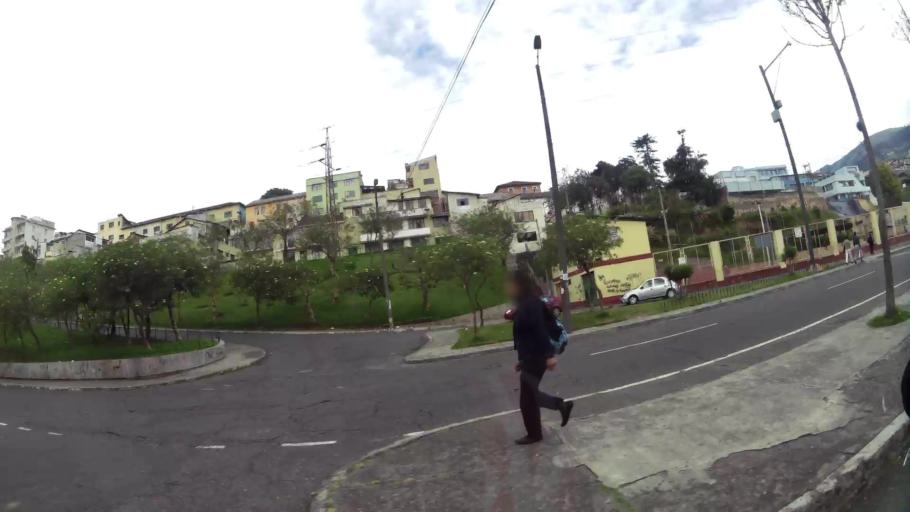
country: EC
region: Pichincha
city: Quito
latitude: -0.2260
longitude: -78.5090
